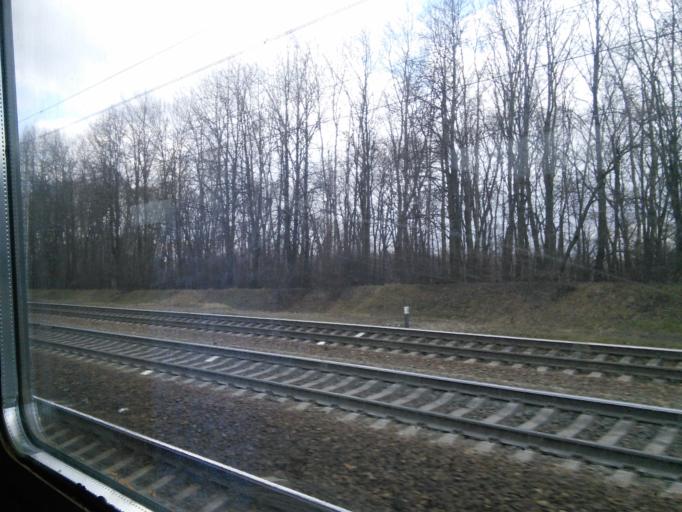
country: RU
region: Moscow
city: Orekhovo-Borisovo Severnoye
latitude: 55.6310
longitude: 37.6849
